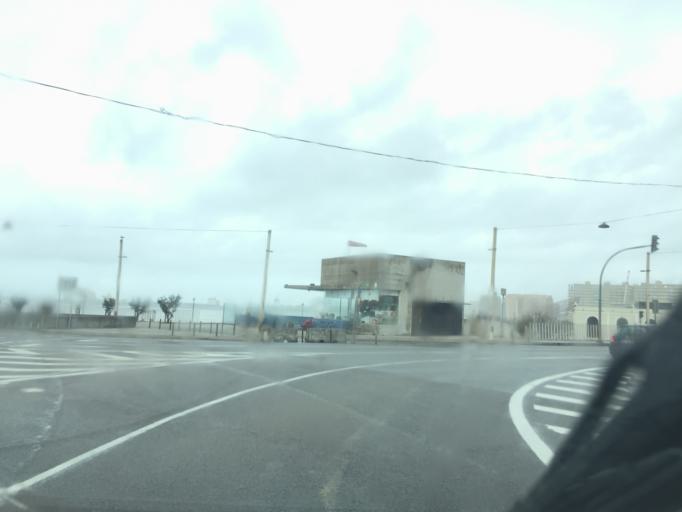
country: PT
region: Porto
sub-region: Matosinhos
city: Matosinhos
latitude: 41.1682
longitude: -8.6880
